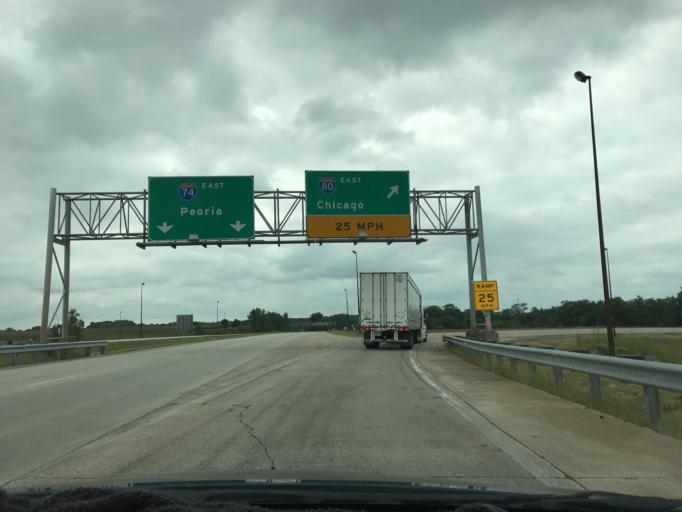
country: US
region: Illinois
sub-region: Henry County
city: Green Rock
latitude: 41.4395
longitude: -90.3299
